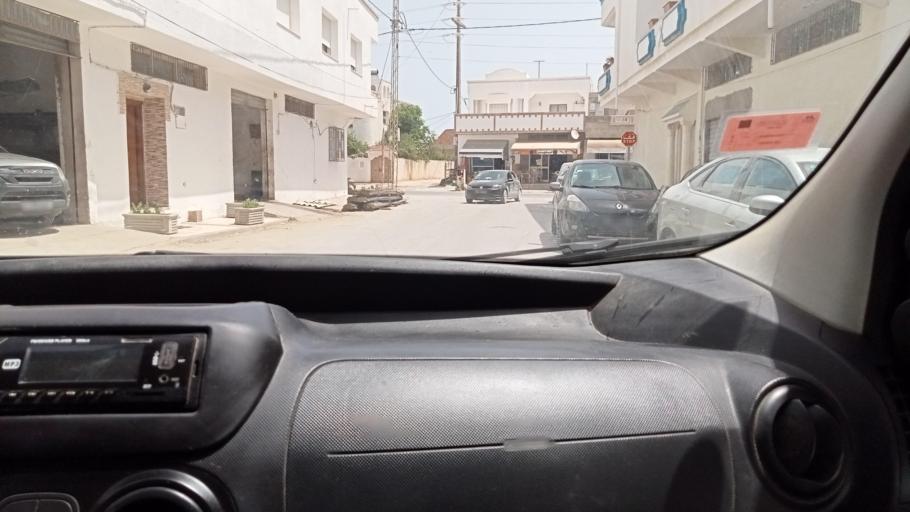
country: TN
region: Nabul
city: Qulaybiyah
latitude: 36.8595
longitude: 11.0898
